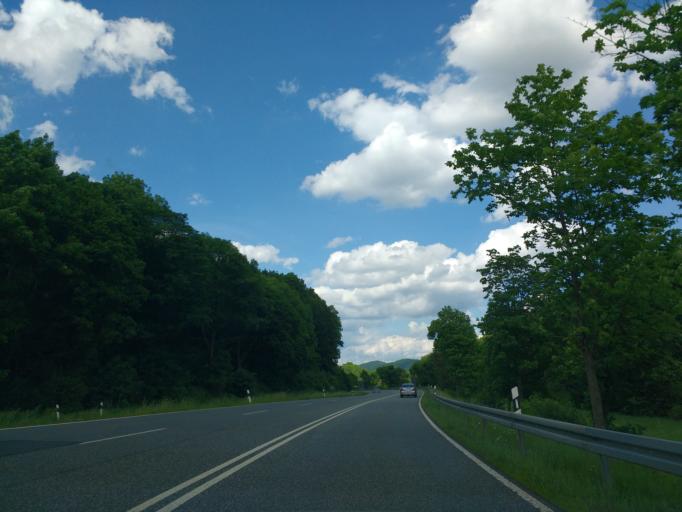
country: DE
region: Hesse
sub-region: Regierungsbezirk Giessen
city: Breidenbach
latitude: 50.8640
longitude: 8.4266
